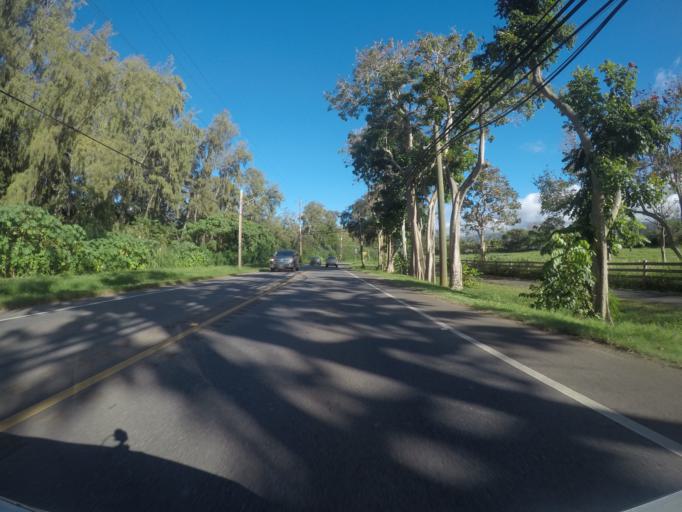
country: US
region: Hawaii
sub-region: Honolulu County
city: La'ie
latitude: 21.6574
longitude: -157.9313
